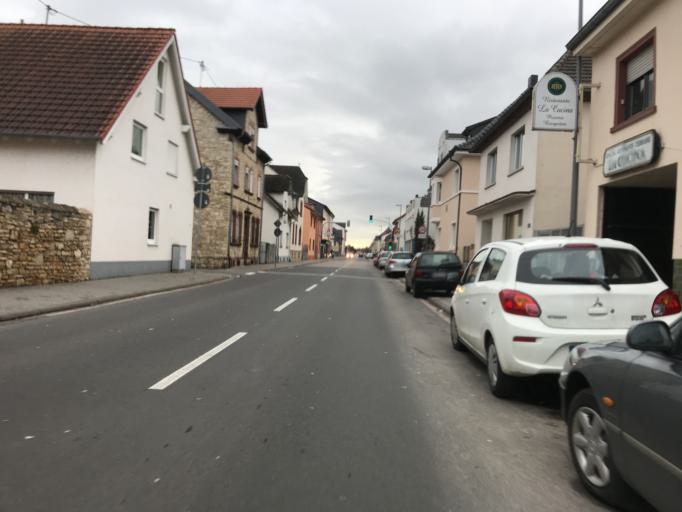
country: DE
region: Rheinland-Pfalz
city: Oestrich-Winkel
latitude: 49.9909
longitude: 8.0239
